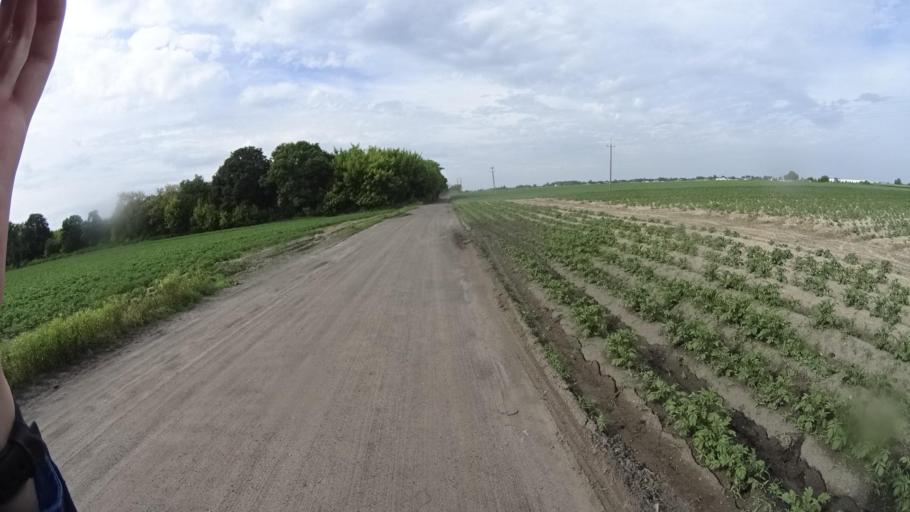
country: PL
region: Masovian Voivodeship
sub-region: Powiat warszawski zachodni
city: Jozefow
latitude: 52.1967
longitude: 20.7423
